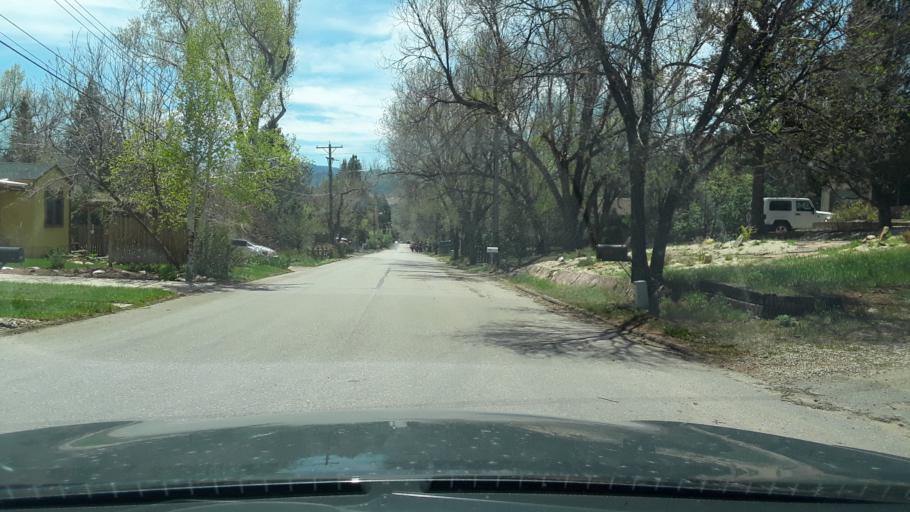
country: US
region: Colorado
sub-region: El Paso County
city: Manitou Springs
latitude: 38.8647
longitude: -104.8848
